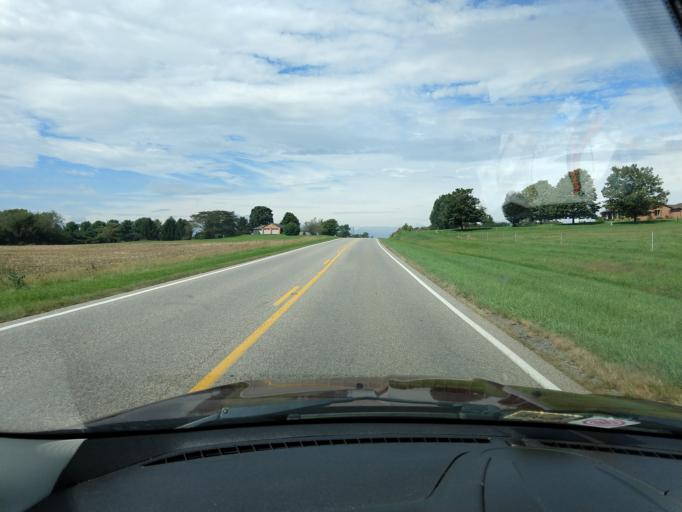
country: US
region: Virginia
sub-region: Augusta County
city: Weyers Cave
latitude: 38.2695
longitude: -78.8772
